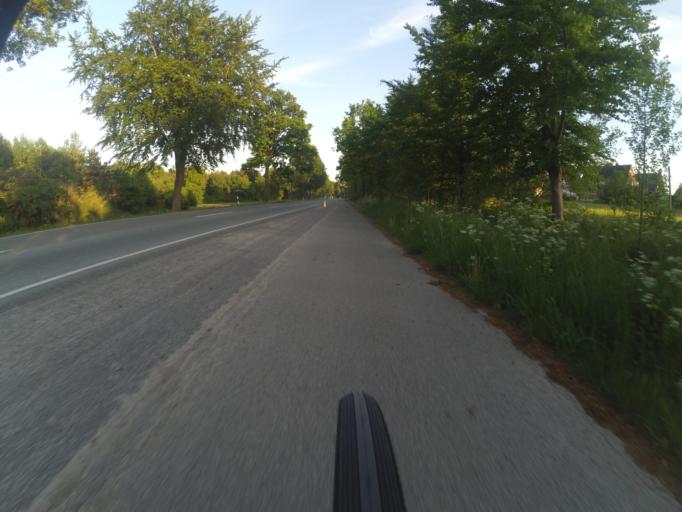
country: DE
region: North Rhine-Westphalia
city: Ibbenburen
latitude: 52.3203
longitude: 7.6719
